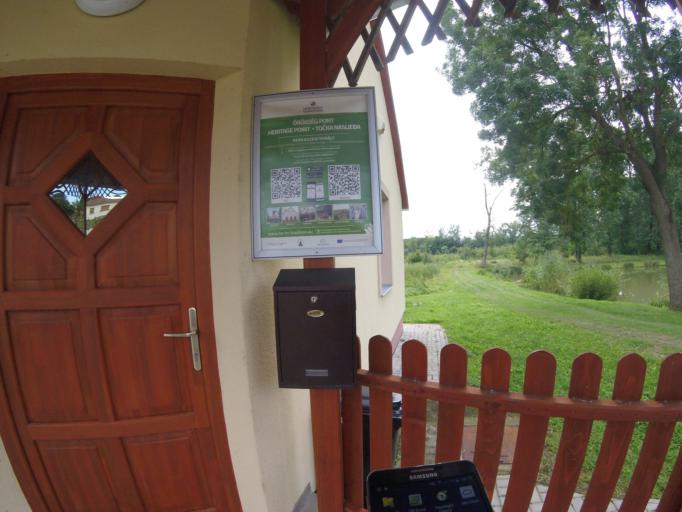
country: HR
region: Medimurska
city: Podturen
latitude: 46.4994
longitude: 16.5836
